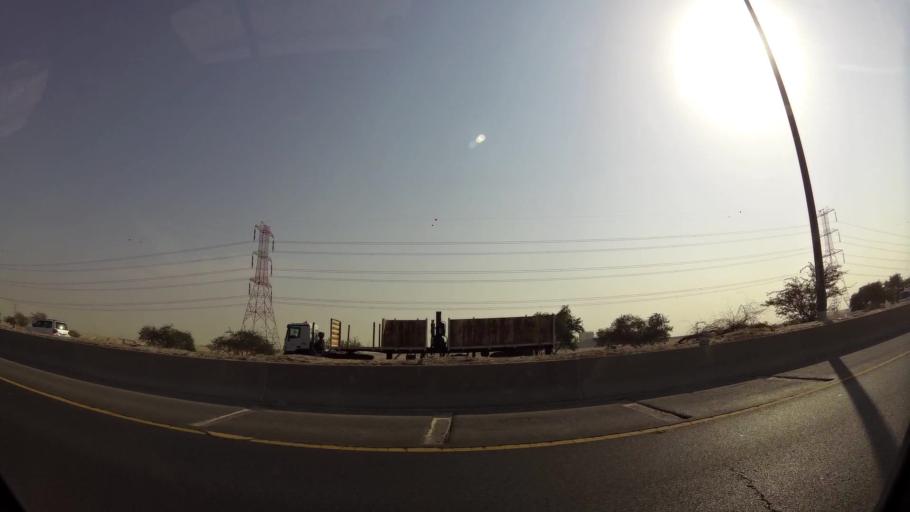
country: KW
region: Al Ahmadi
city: Al Ahmadi
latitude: 29.0192
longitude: 48.0920
